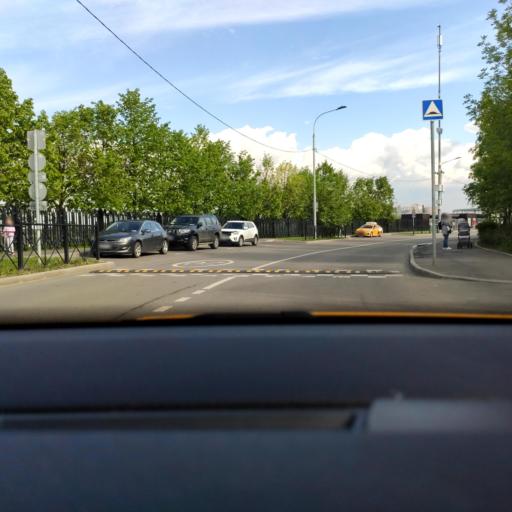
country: RU
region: Moskovskaya
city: Pavshino
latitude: 55.8365
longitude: 37.3600
